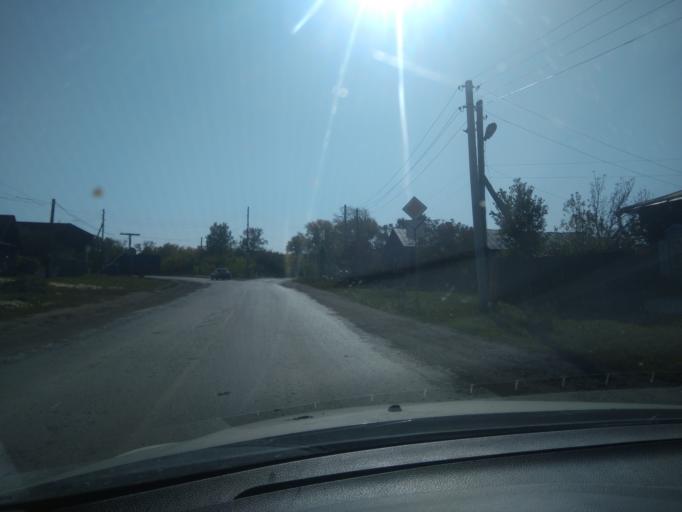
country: RU
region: Sverdlovsk
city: Pokrovskoye
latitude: 56.4663
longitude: 61.6151
